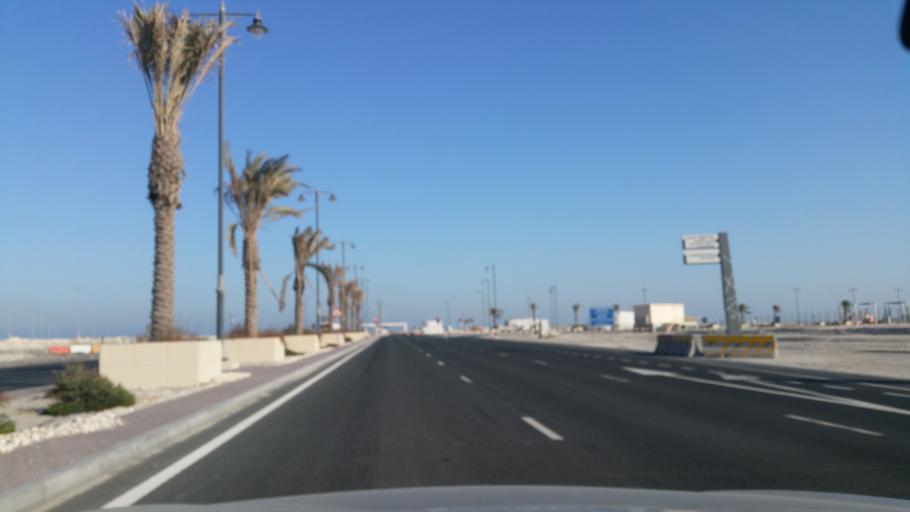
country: QA
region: Al Wakrah
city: Umm Sa'id
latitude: 25.0555
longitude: 51.6000
